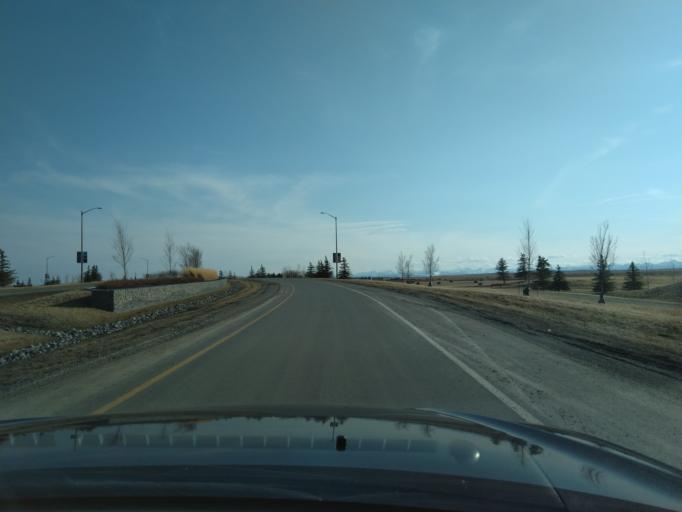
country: CA
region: Alberta
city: Cochrane
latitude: 51.1083
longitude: -114.3918
